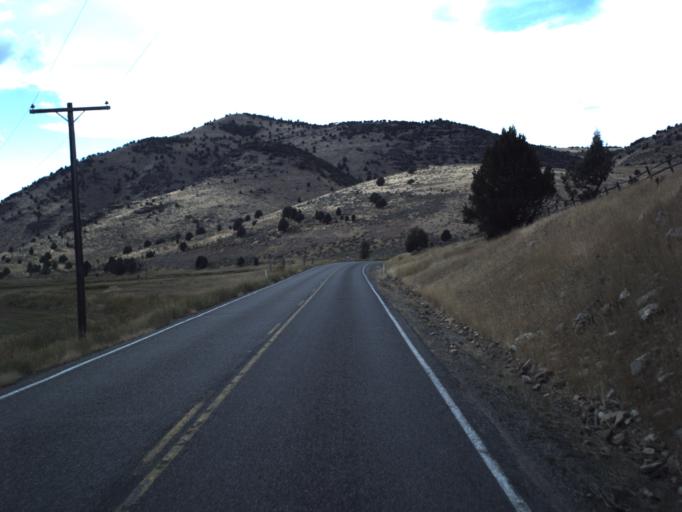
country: US
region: Utah
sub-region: Cache County
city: Millville
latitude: 41.6036
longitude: -111.5766
